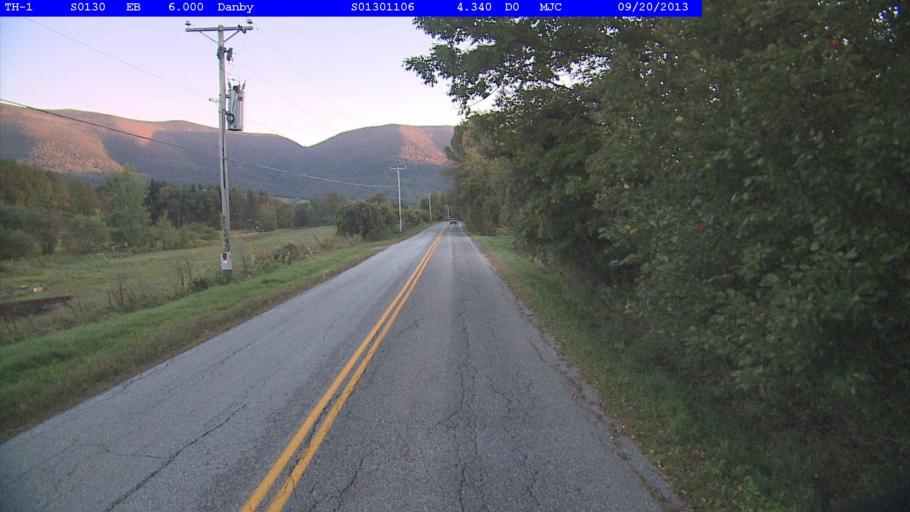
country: US
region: Vermont
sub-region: Bennington County
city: Manchester Center
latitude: 43.3529
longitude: -73.0483
